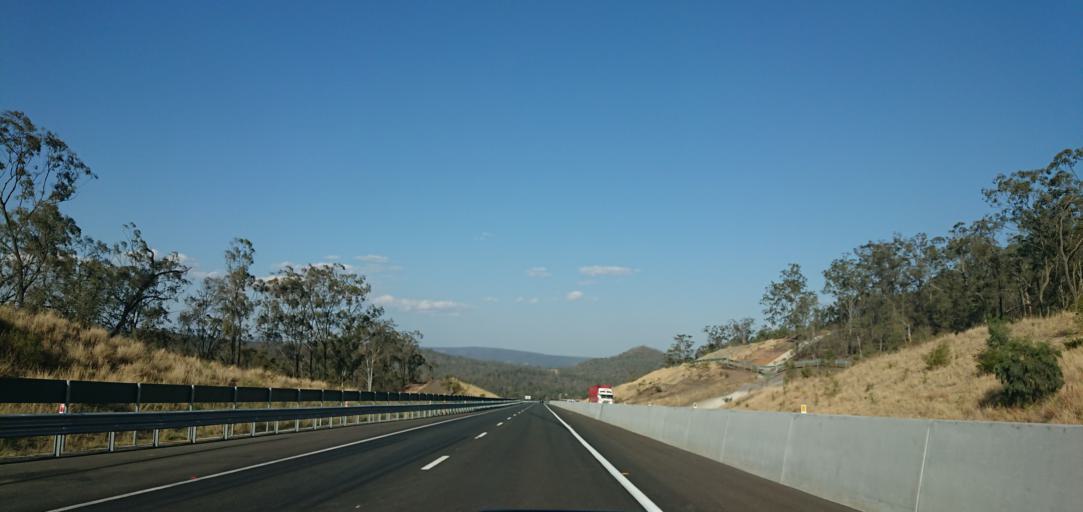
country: AU
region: Queensland
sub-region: Toowoomba
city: East Toowoomba
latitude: -27.5072
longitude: 152.0021
